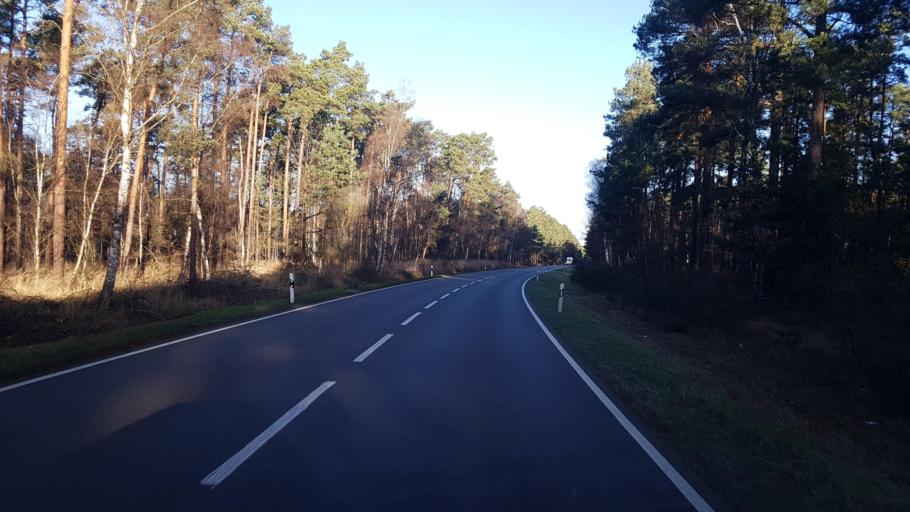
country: DE
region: Brandenburg
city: Heinersbruck
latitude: 51.7174
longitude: 14.4585
